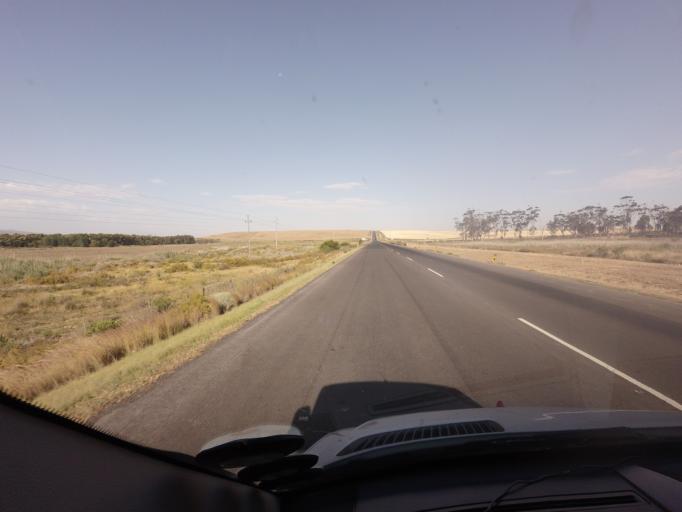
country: ZA
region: Western Cape
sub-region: Cape Winelands District Municipality
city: Ashton
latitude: -34.1556
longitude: 19.9386
